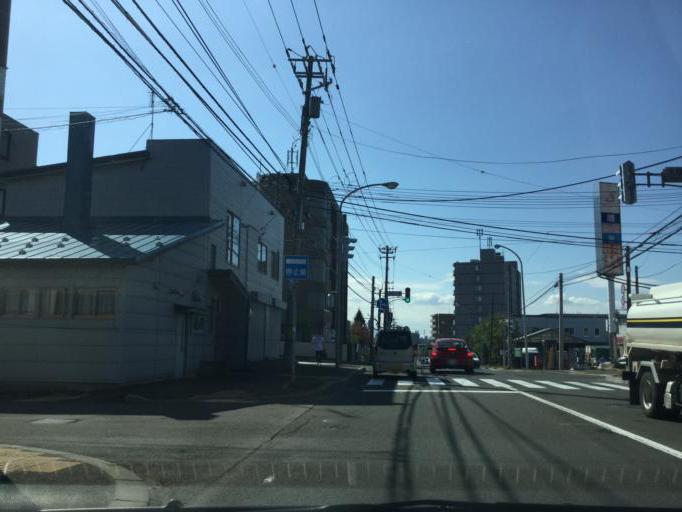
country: JP
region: Hokkaido
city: Sapporo
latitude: 43.0206
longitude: 141.4478
